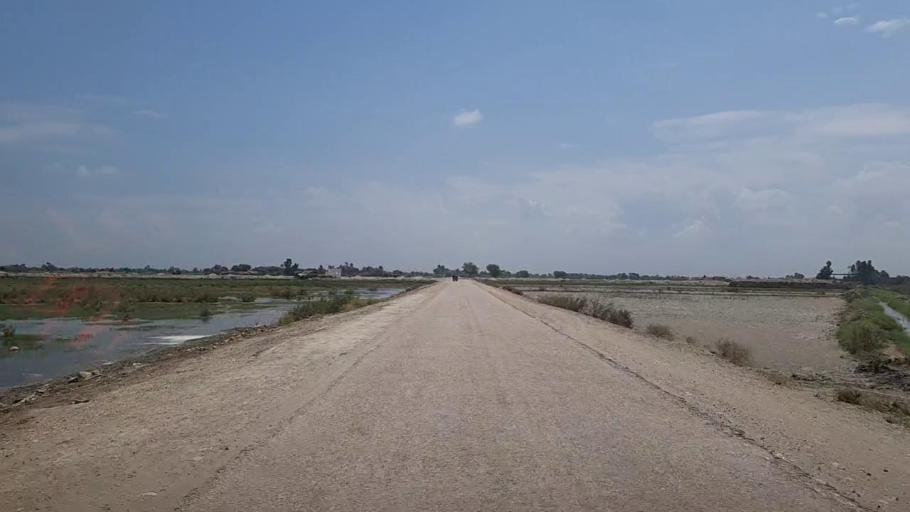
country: PK
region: Sindh
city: Kandhkot
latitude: 28.2785
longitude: 69.1756
